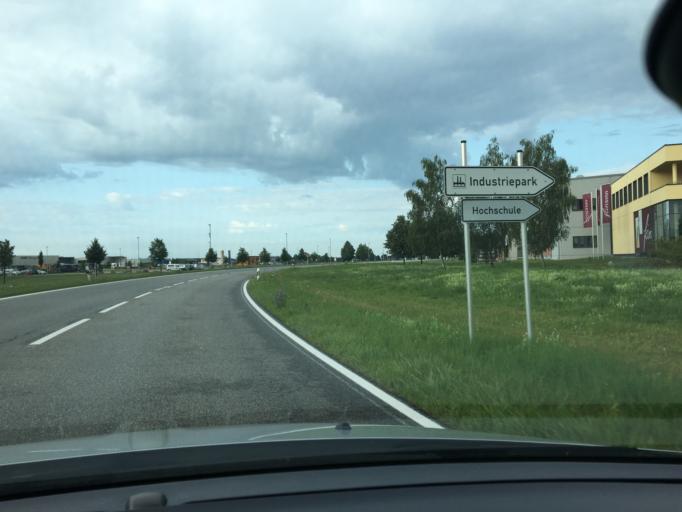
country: DE
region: Bavaria
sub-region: Upper Bavaria
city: Muehldorf
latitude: 48.2561
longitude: 12.5465
